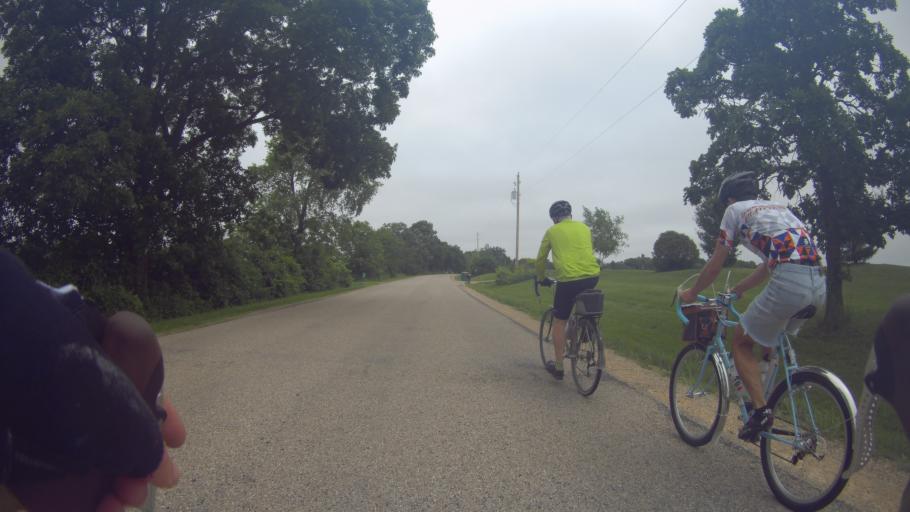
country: US
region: Wisconsin
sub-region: Green County
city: Brooklyn
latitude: 42.8625
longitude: -89.4135
